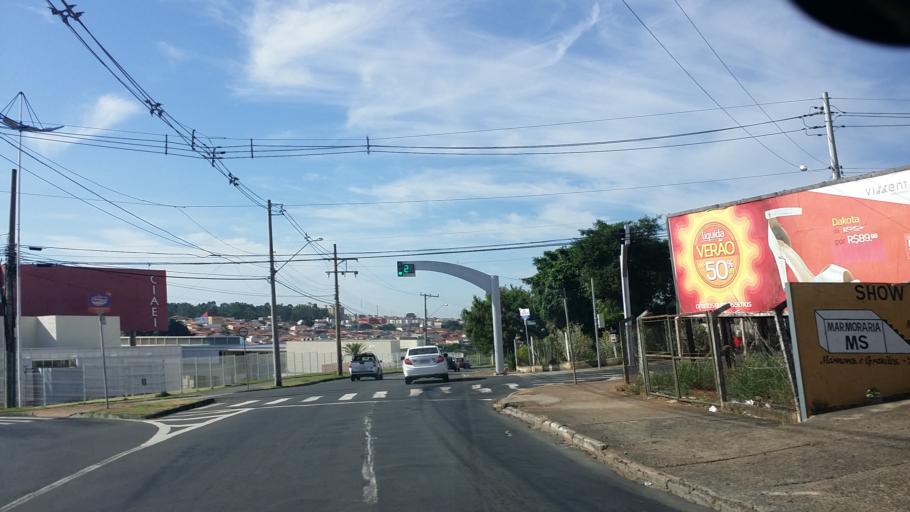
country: BR
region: Sao Paulo
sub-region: Indaiatuba
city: Indaiatuba
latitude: -23.0979
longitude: -47.2289
